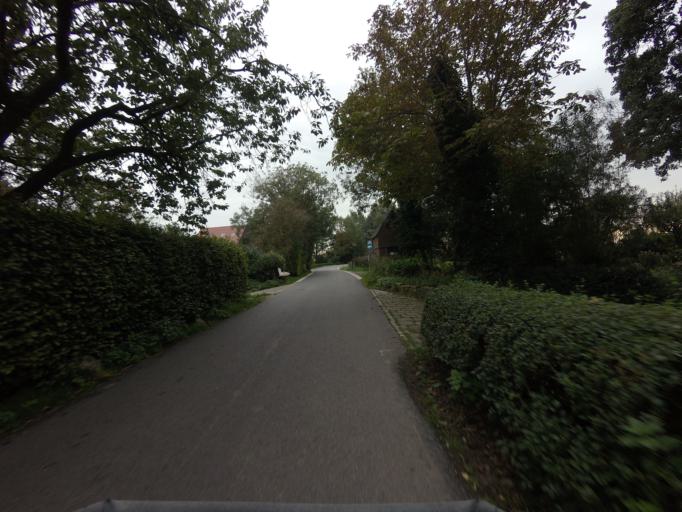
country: NL
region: Friesland
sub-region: Sudwest Fryslan
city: IJlst
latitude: 53.0105
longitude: 5.5841
